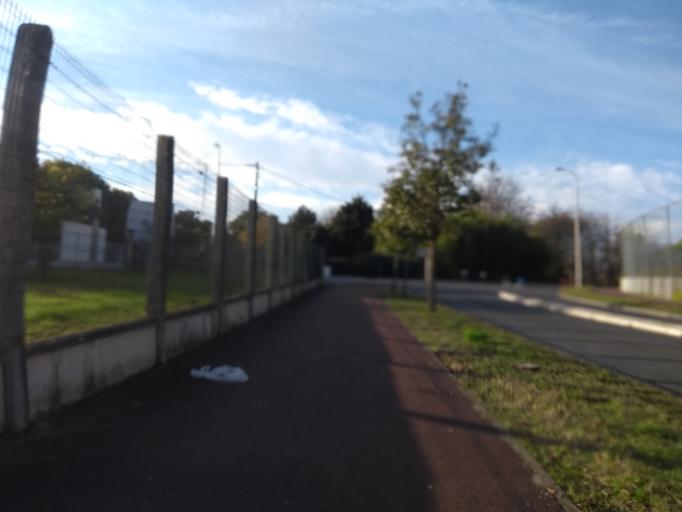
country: FR
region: Aquitaine
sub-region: Departement de la Gironde
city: Pessac
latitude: 44.7978
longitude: -0.6226
